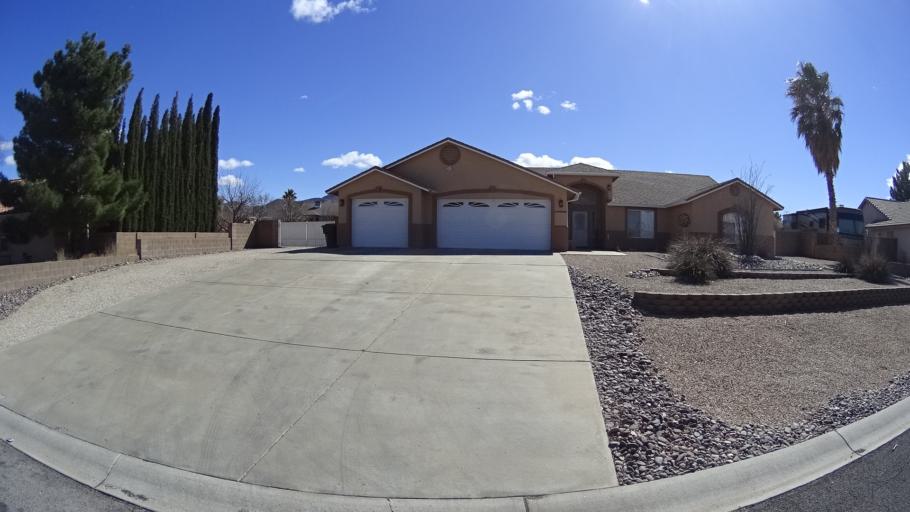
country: US
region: Arizona
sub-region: Mohave County
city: Kingman
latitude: 35.1999
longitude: -113.9737
